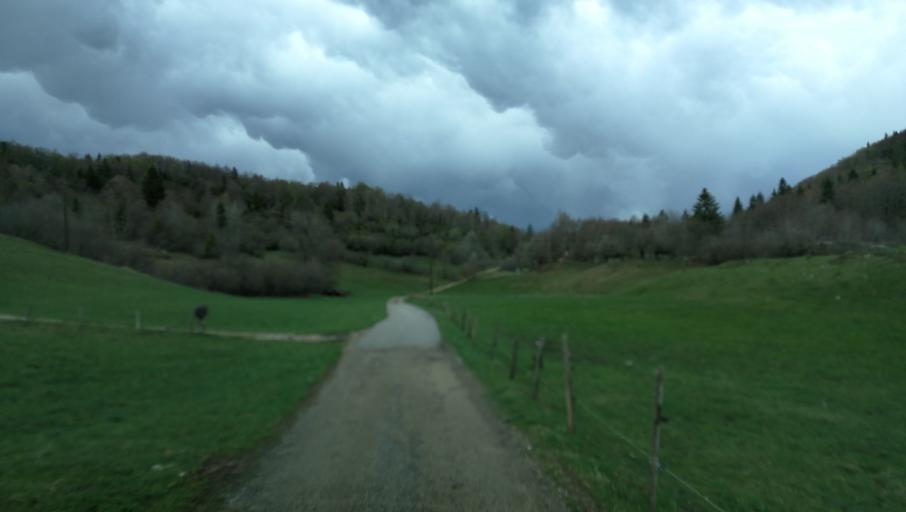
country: FR
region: Franche-Comte
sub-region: Departement du Jura
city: Lavans-les-Saint-Claude
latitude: 46.3184
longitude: 5.8088
